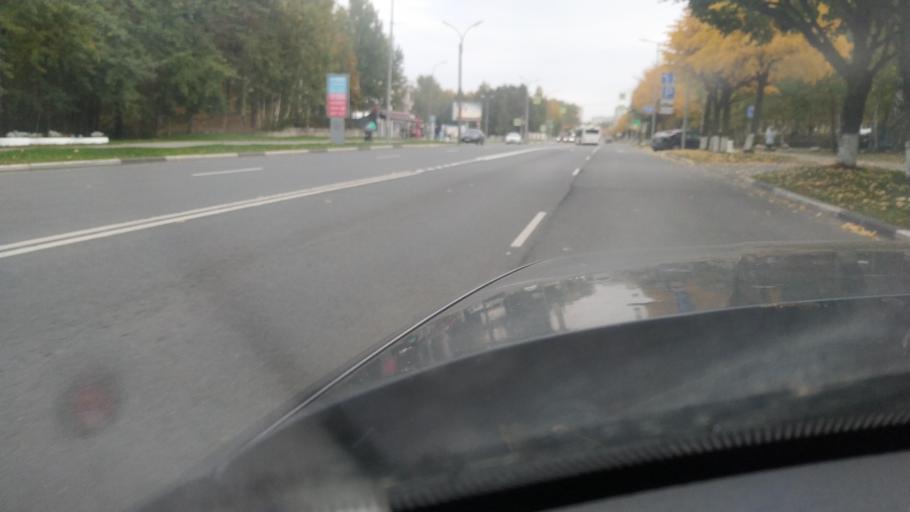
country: RU
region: Leningrad
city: Sosnovyy Bor
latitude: 59.8987
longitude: 29.0854
